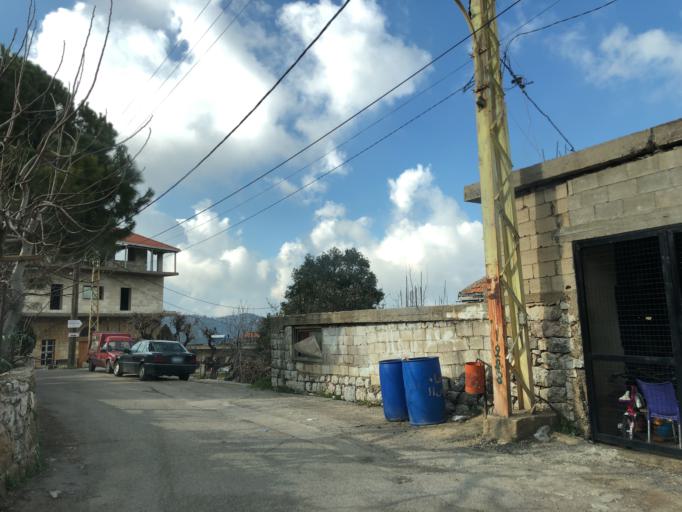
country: LB
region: Liban-Nord
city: Amioun
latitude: 34.2058
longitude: 35.8418
